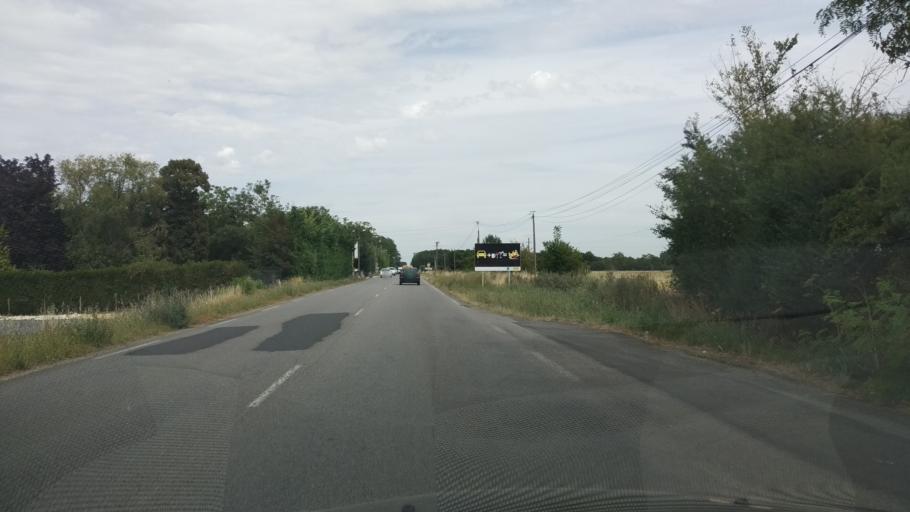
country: FR
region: Poitou-Charentes
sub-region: Departement de la Vienne
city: Mignaloux-Beauvoir
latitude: 46.5632
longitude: 0.4114
